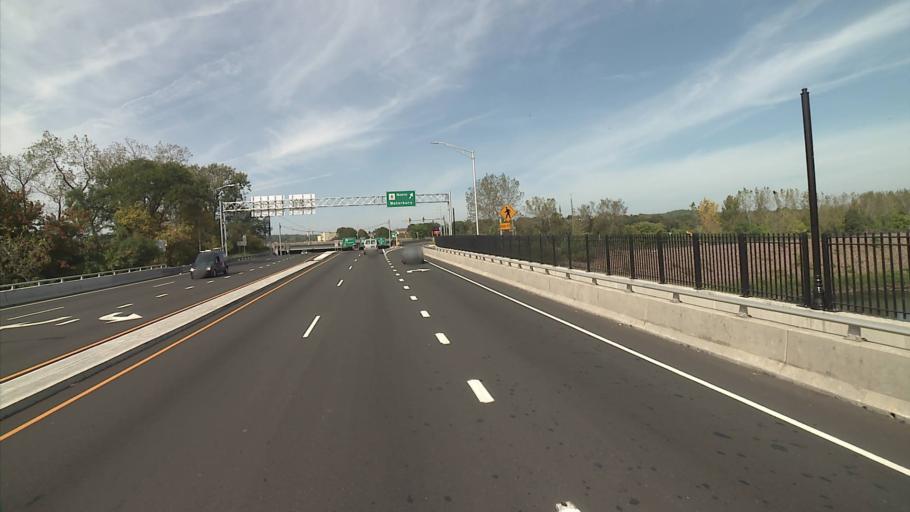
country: US
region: Connecticut
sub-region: New Haven County
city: Derby
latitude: 41.3190
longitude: -73.0821
